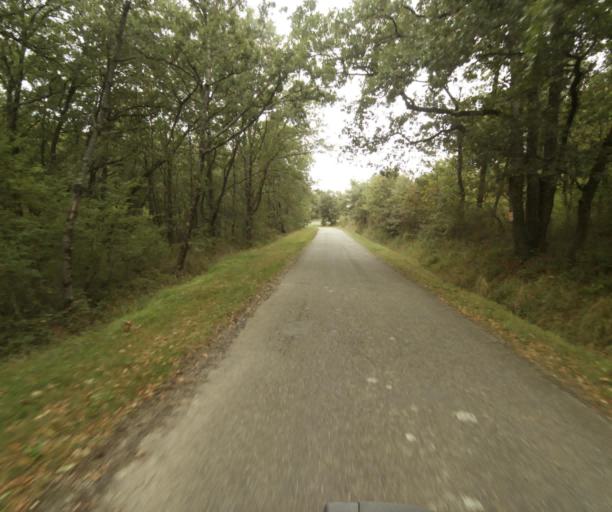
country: FR
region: Midi-Pyrenees
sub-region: Departement du Tarn-et-Garonne
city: Beaumont-de-Lomagne
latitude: 43.8435
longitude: 1.0985
